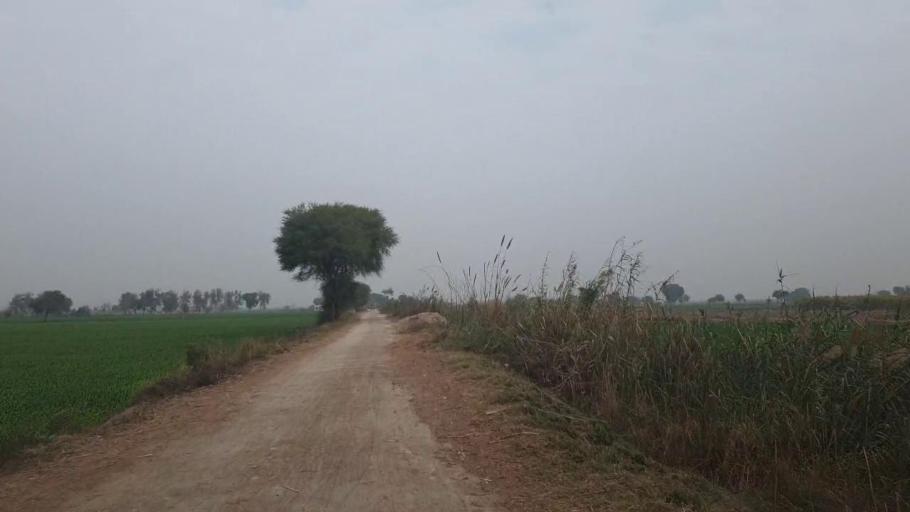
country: PK
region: Sindh
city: Tando Adam
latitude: 25.7256
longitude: 68.7386
